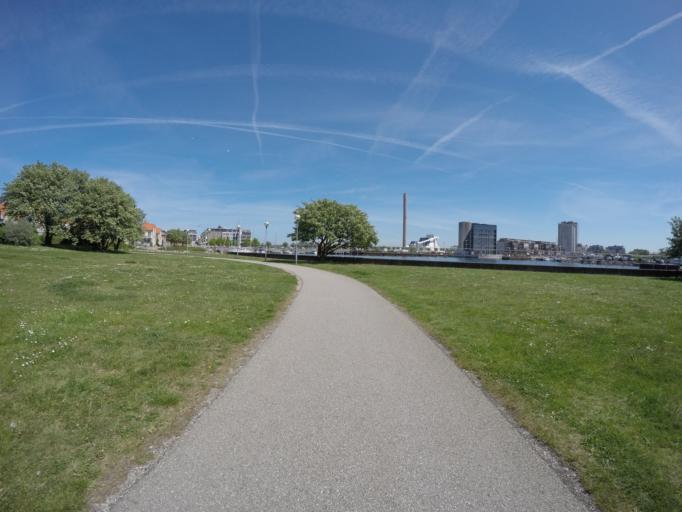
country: SE
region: Skane
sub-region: Malmo
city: Bunkeflostrand
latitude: 55.5875
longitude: 12.9202
